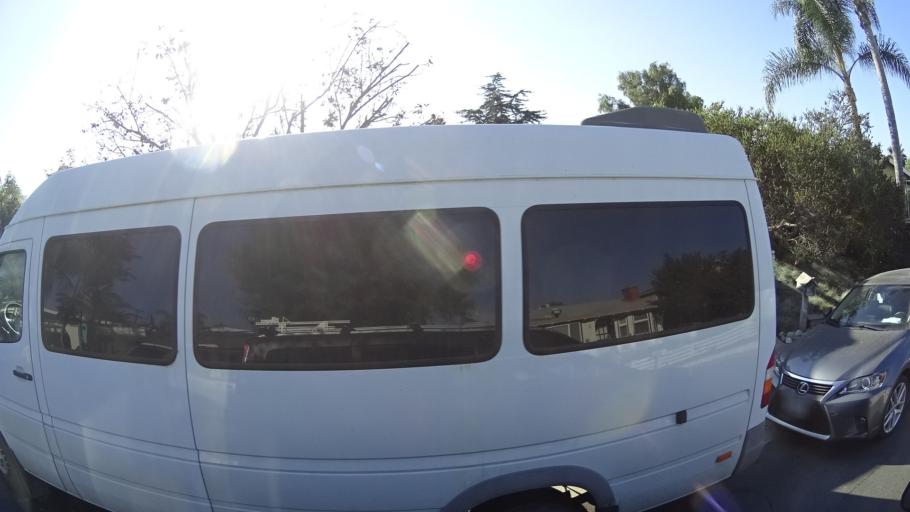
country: US
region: California
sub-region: Orange County
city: San Clemente
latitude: 33.4145
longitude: -117.6014
